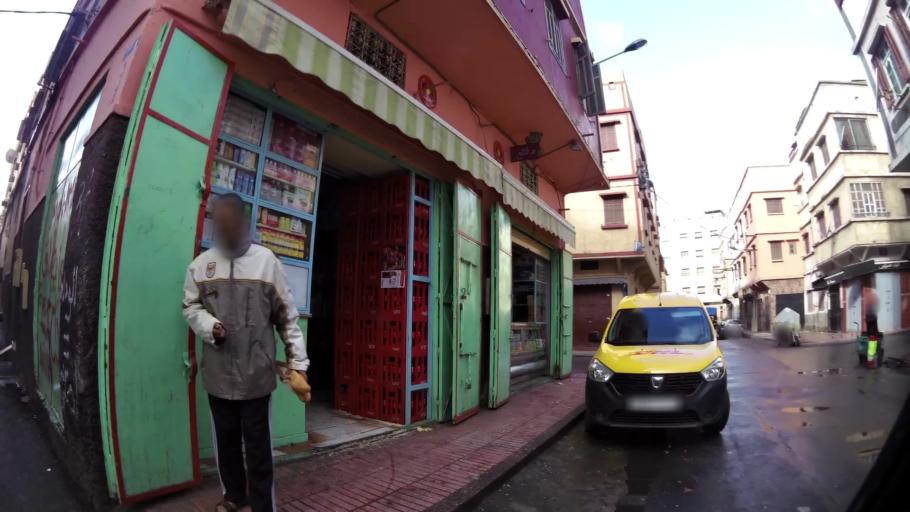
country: MA
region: Grand Casablanca
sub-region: Casablanca
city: Casablanca
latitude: 33.5646
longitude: -7.5855
